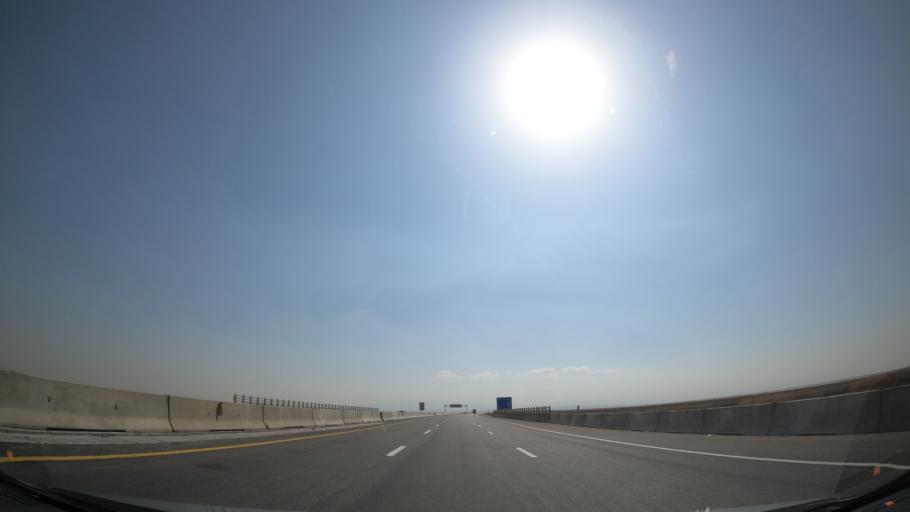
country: IR
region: Qazvin
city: Abyek
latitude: 35.9488
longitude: 50.4673
